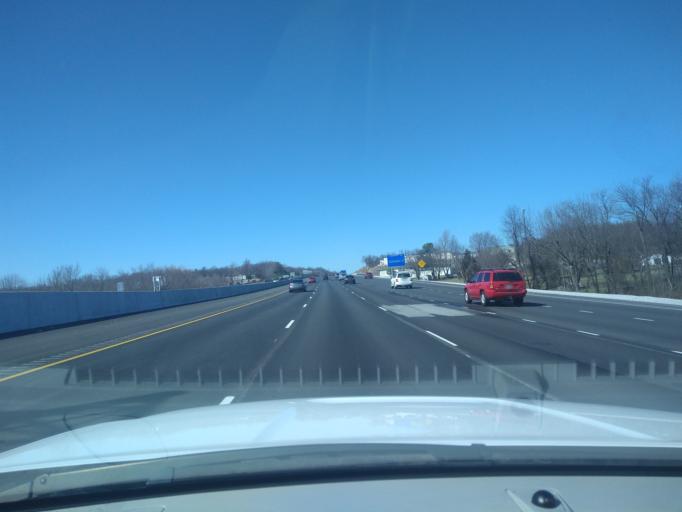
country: US
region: Arkansas
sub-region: Washington County
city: Johnson
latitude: 36.1149
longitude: -94.1761
